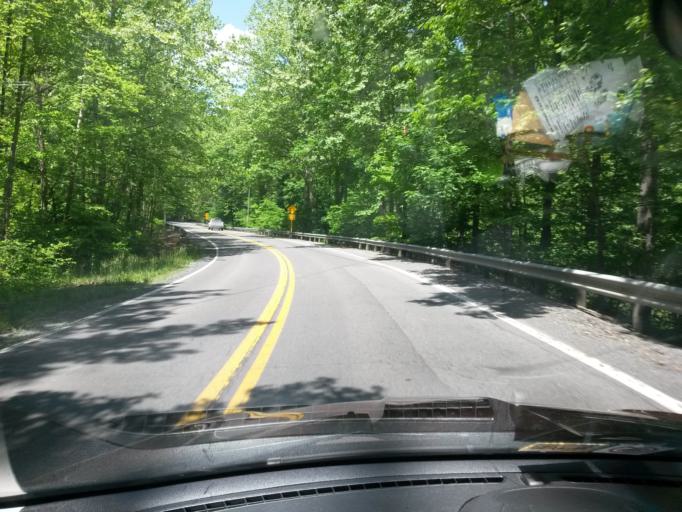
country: US
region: West Virginia
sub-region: Wyoming County
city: Pineville
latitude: 37.5162
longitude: -81.5811
